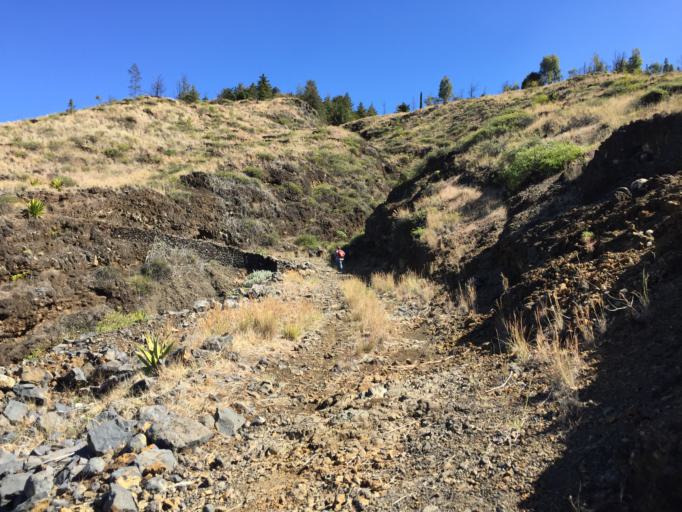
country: CV
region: Mosteiros
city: Porto dos Mosteiros
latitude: 15.0065
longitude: -24.3583
